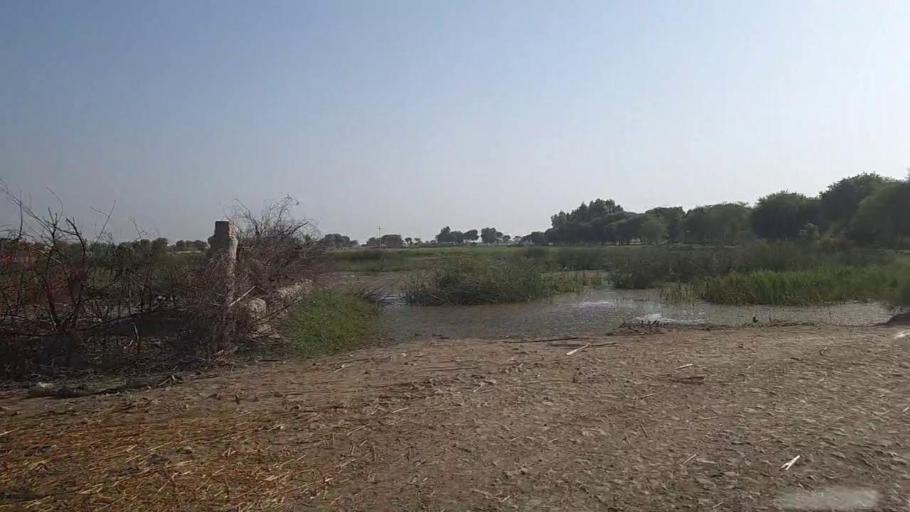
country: PK
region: Sindh
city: Kandhkot
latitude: 28.3551
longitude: 69.3353
